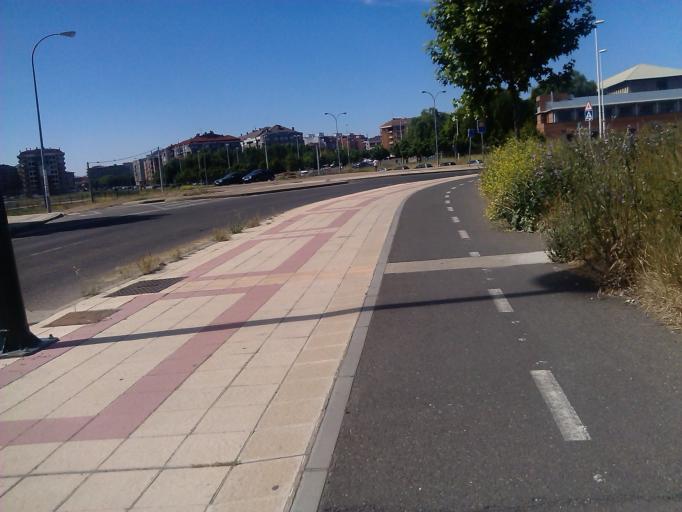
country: ES
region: Castille and Leon
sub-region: Provincia de Leon
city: Leon
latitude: 42.6100
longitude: -5.5628
